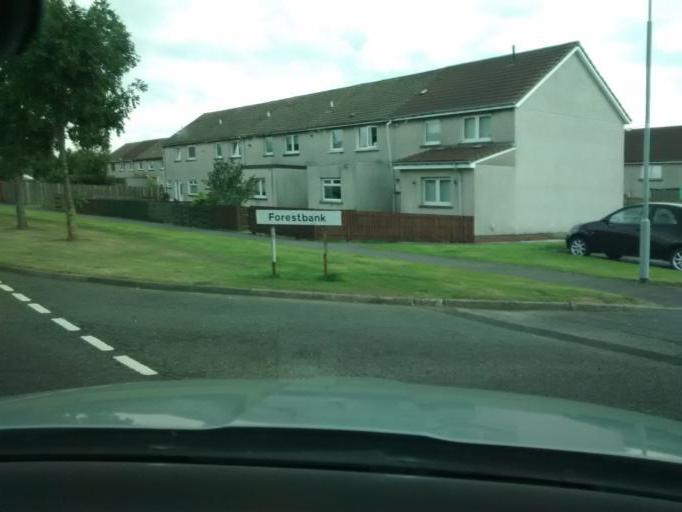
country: GB
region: Scotland
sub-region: West Lothian
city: Livingston
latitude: 55.8988
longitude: -3.5135
